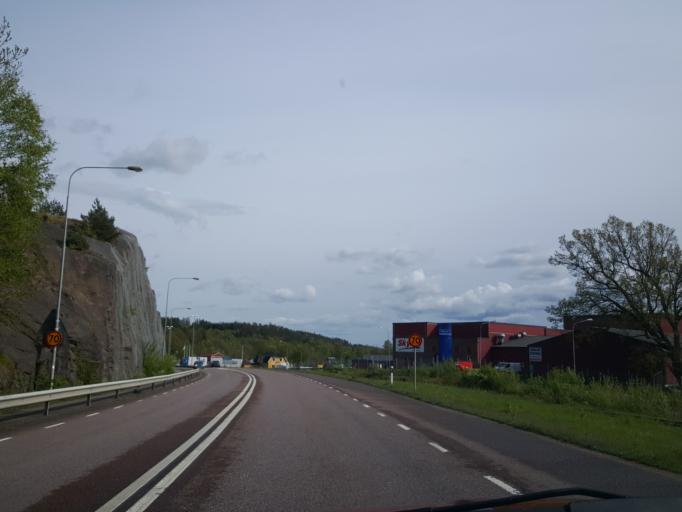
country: SE
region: Vaestra Goetaland
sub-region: Lilla Edets Kommun
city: Lilla Edet
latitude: 58.1105
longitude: 12.1441
